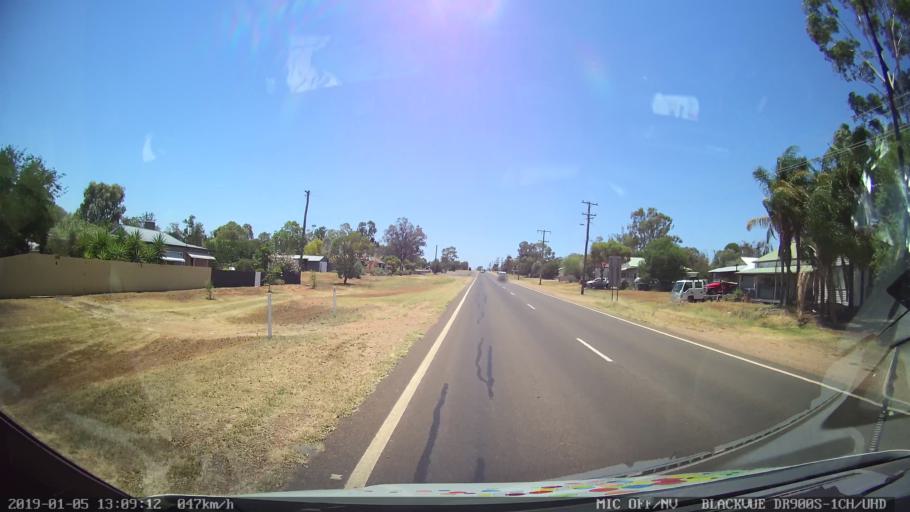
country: AU
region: New South Wales
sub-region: Gunnedah
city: Gunnedah
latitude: -31.0986
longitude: 149.9086
